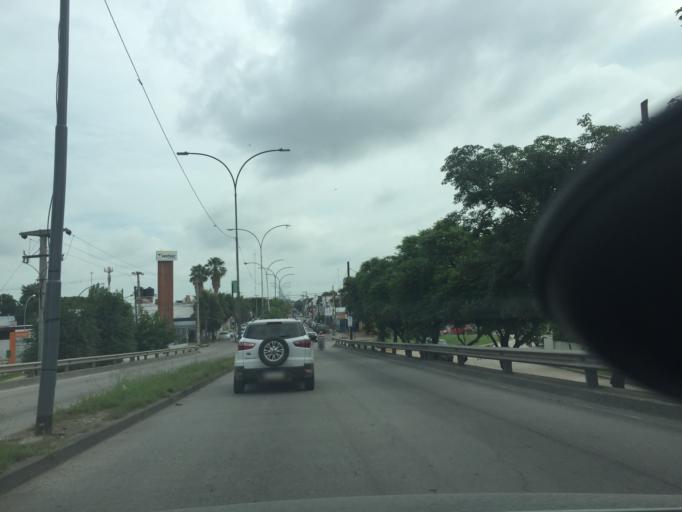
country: AR
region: Cordoba
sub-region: Departamento de Capital
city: Cordoba
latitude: -31.4444
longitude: -64.1980
